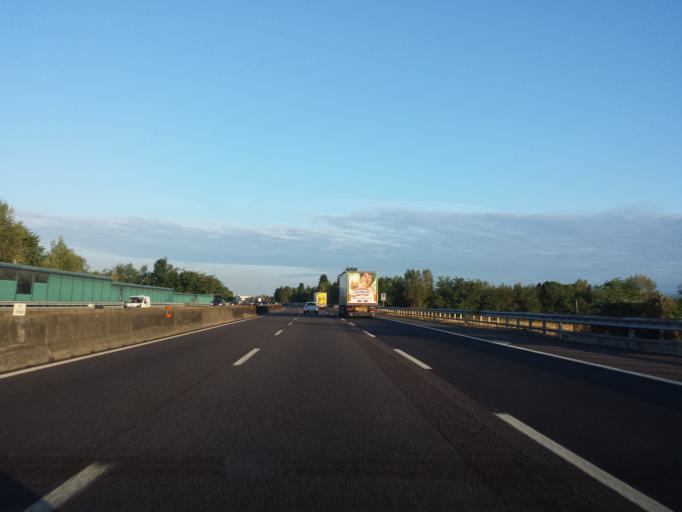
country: IT
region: Lombardy
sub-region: Provincia di Brescia
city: Ospitaletto
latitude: 45.5602
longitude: 10.0927
